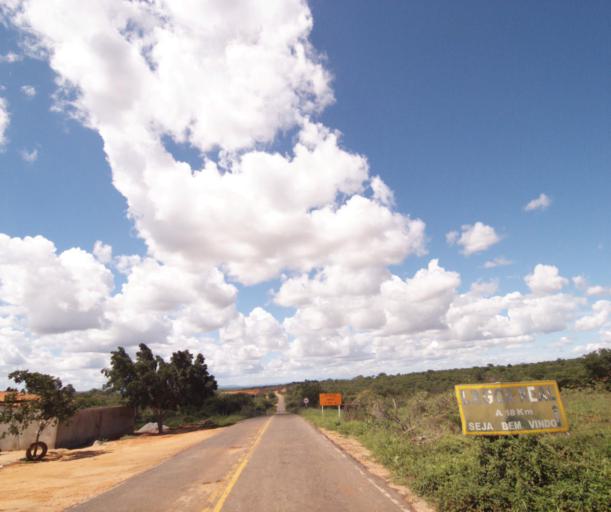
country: BR
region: Bahia
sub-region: Caetite
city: Caetite
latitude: -14.1722
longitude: -42.1852
